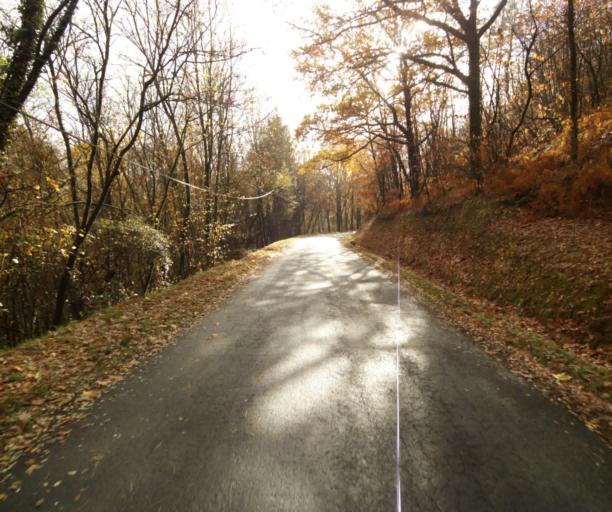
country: FR
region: Limousin
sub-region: Departement de la Correze
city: Cornil
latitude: 45.2113
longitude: 1.6485
